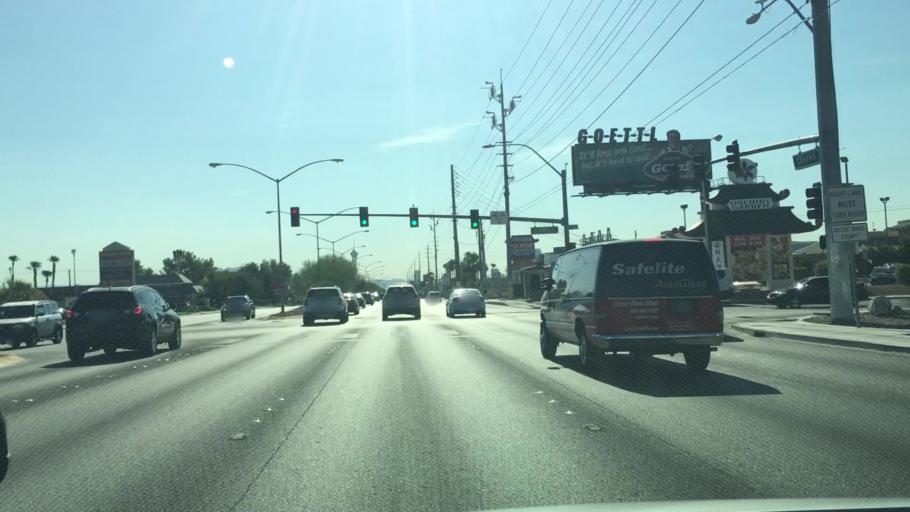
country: US
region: Nevada
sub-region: Clark County
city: Spring Valley
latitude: 36.1443
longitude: -115.2171
